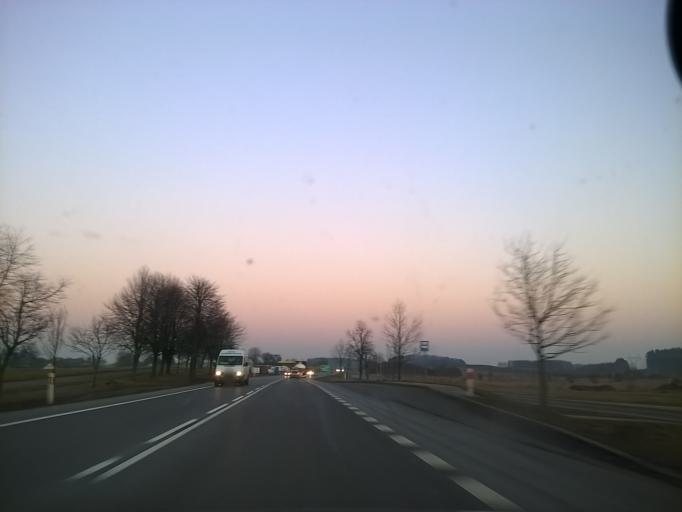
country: PL
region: Warmian-Masurian Voivodeship
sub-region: Powiat olsztynski
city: Olsztyn
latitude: 53.7865
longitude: 20.5869
